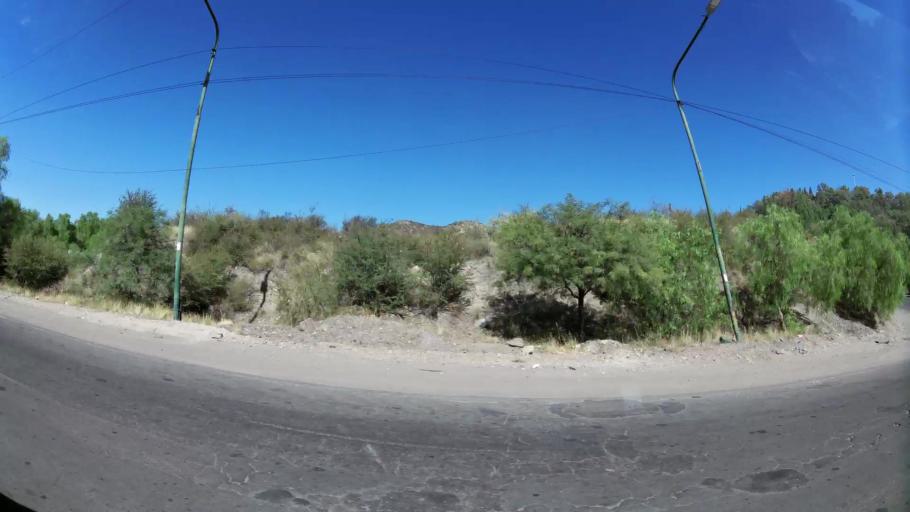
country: AR
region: Mendoza
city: Mendoza
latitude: -32.8914
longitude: -68.8854
